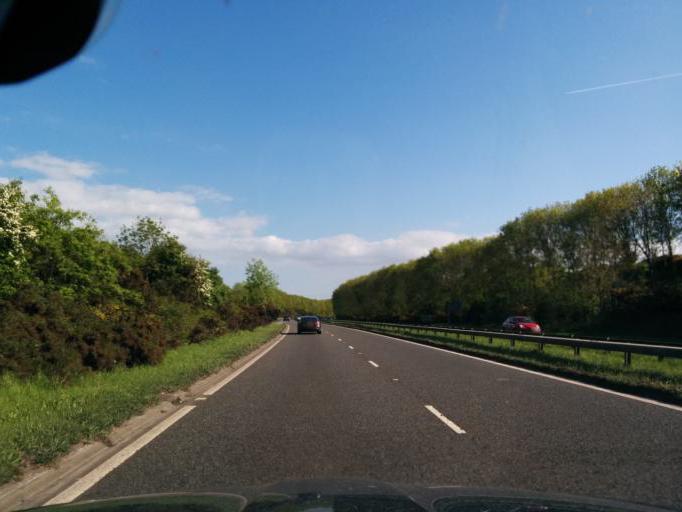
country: GB
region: England
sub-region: Northumberland
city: Bedlington
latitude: 55.1265
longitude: -1.5565
